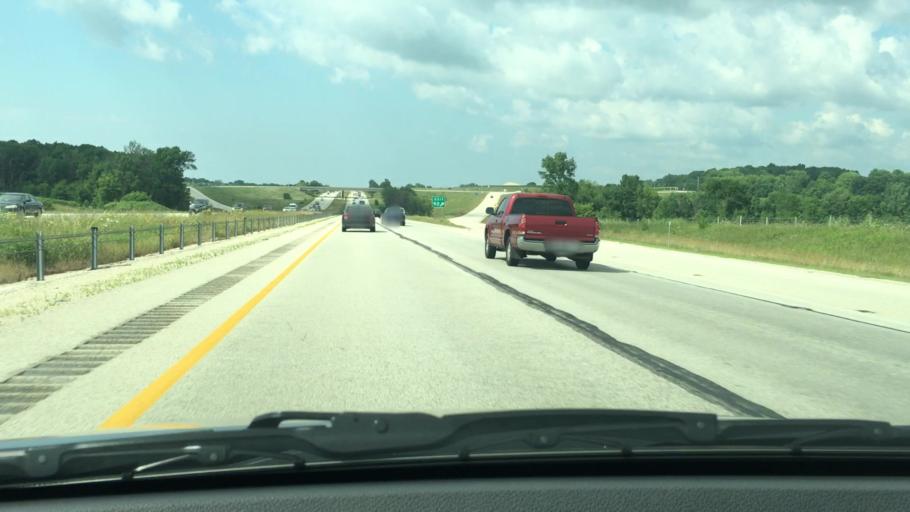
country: US
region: Wisconsin
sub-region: Fond du Lac County
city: Fond du Lac
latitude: 43.6833
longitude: -88.4418
